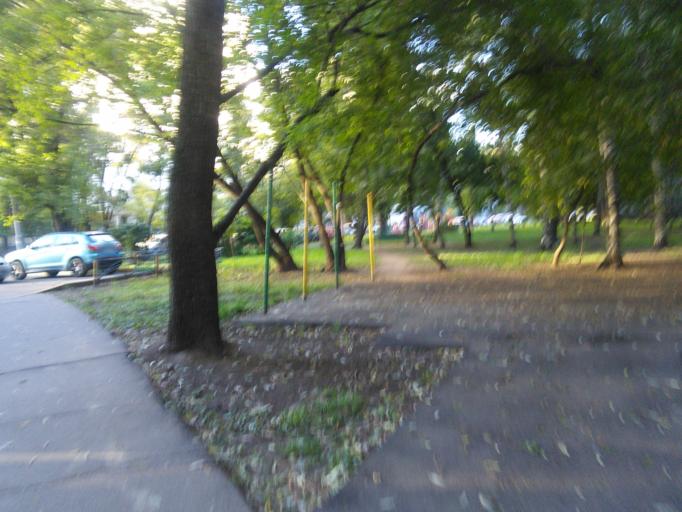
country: RU
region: Moskovskaya
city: Levoberezhnyy
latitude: 55.8472
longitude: 37.4445
